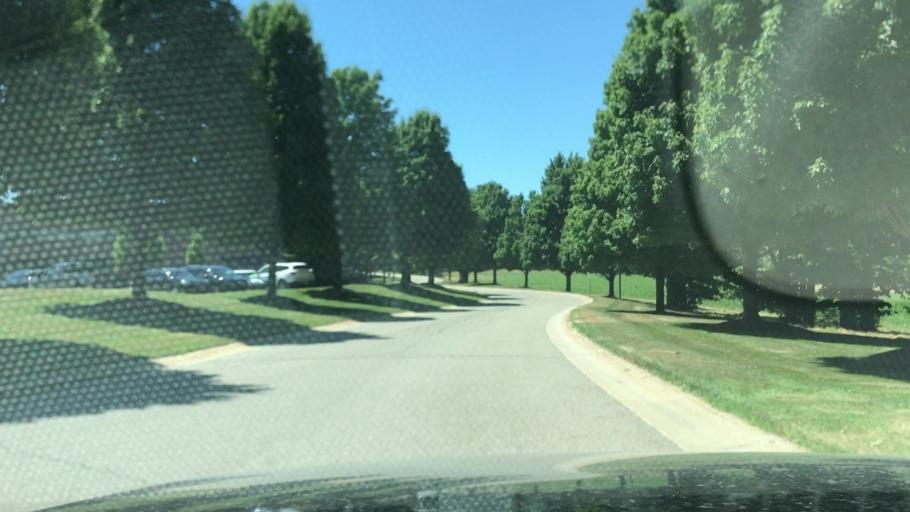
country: US
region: Michigan
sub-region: Ottawa County
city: Holland
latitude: 42.7721
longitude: -86.0731
